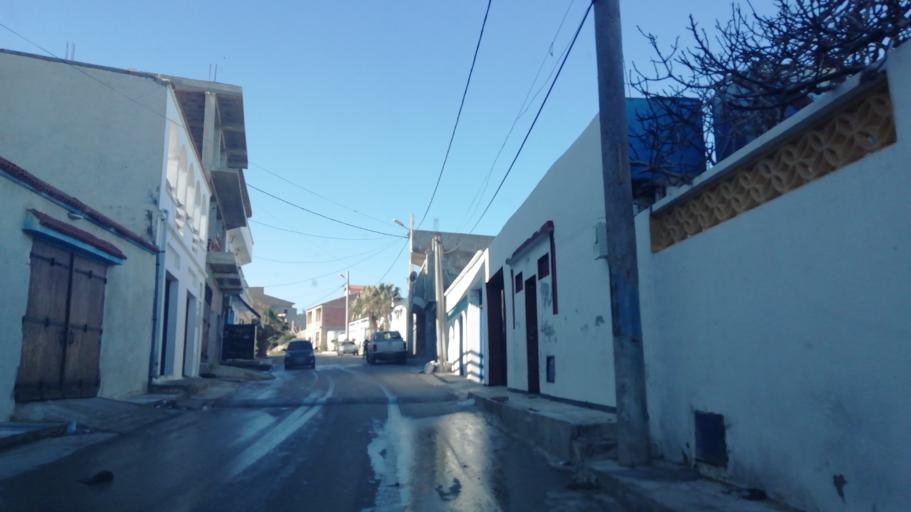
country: DZ
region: Oran
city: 'Ain el Turk
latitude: 35.7226
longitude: -0.8508
